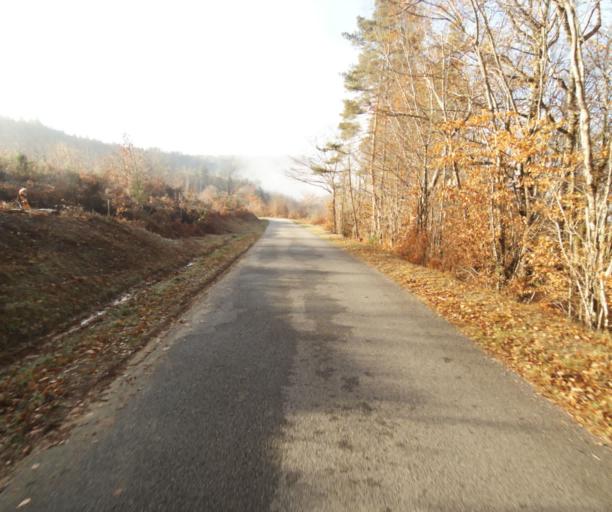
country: FR
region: Limousin
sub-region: Departement de la Correze
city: Laguenne
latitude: 45.2616
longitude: 1.7924
